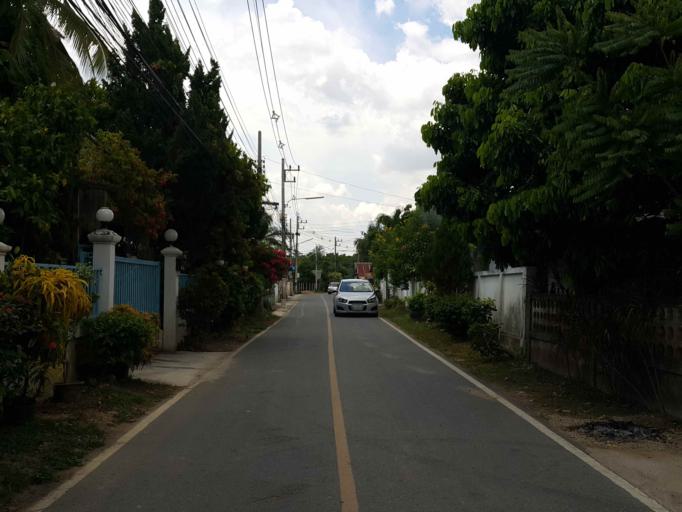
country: TH
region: Chiang Mai
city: Chiang Mai
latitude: 18.7431
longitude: 98.9854
